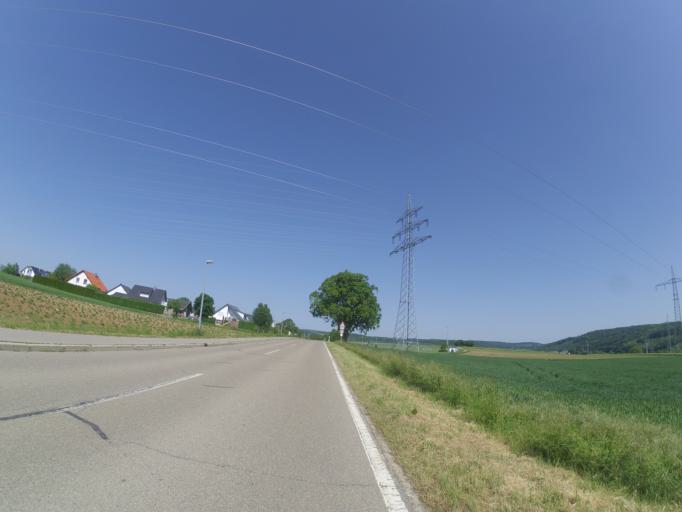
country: DE
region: Baden-Wuerttemberg
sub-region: Tuebingen Region
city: Amstetten
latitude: 48.5749
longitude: 9.8615
